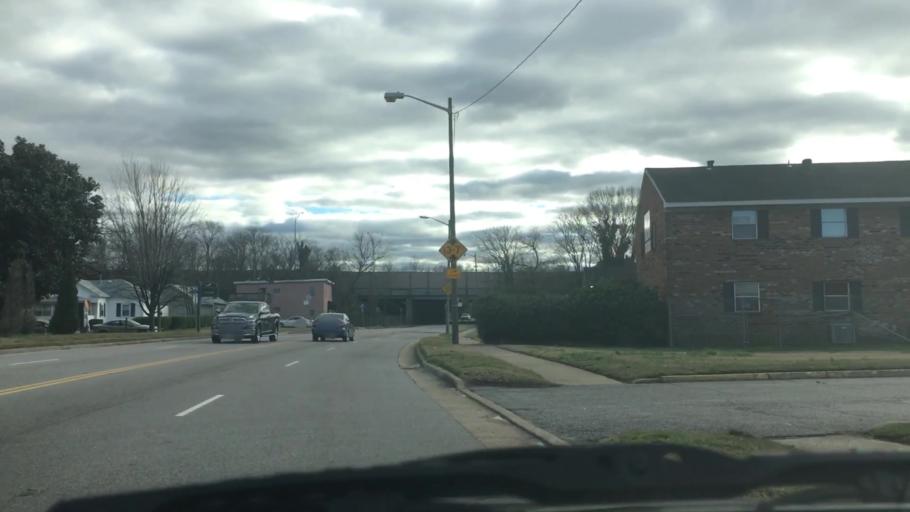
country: US
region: Virginia
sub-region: City of Norfolk
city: Norfolk
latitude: 36.9050
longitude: -76.2432
